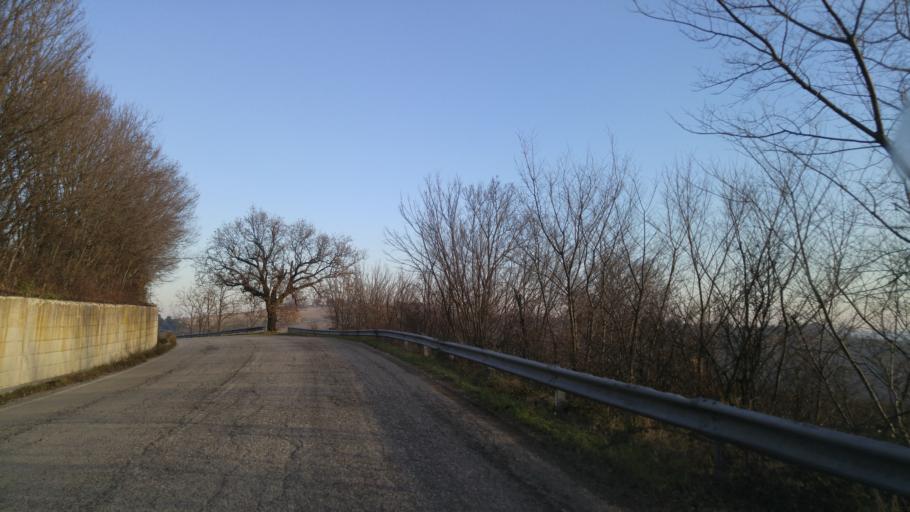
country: IT
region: The Marches
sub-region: Provincia di Pesaro e Urbino
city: San Giorgio di Pesaro
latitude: 43.7102
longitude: 13.0029
